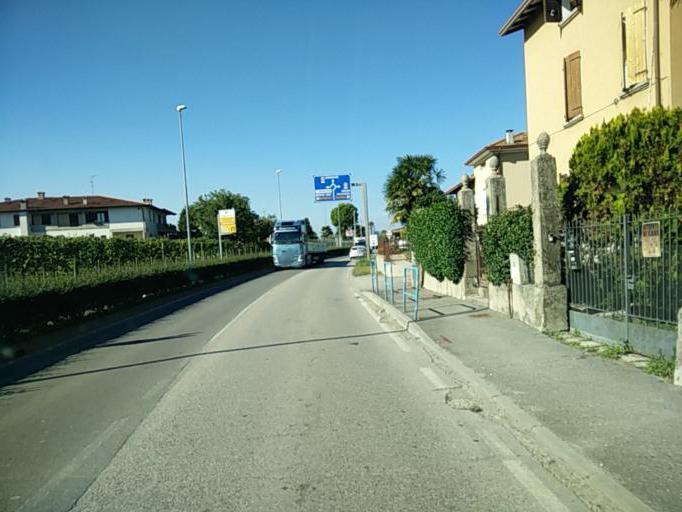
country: IT
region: Lombardy
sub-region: Provincia di Brescia
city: San Martino della Battaglia
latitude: 45.4436
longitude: 10.5965
